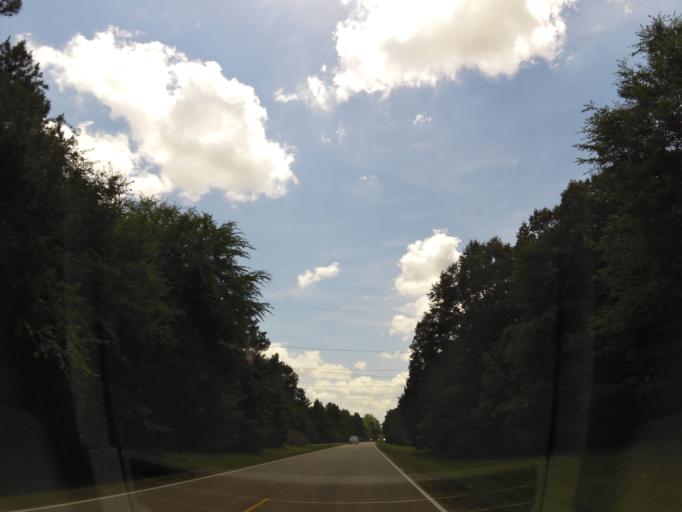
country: US
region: Mississippi
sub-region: Lee County
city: Tupelo
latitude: 34.2441
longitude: -88.7605
